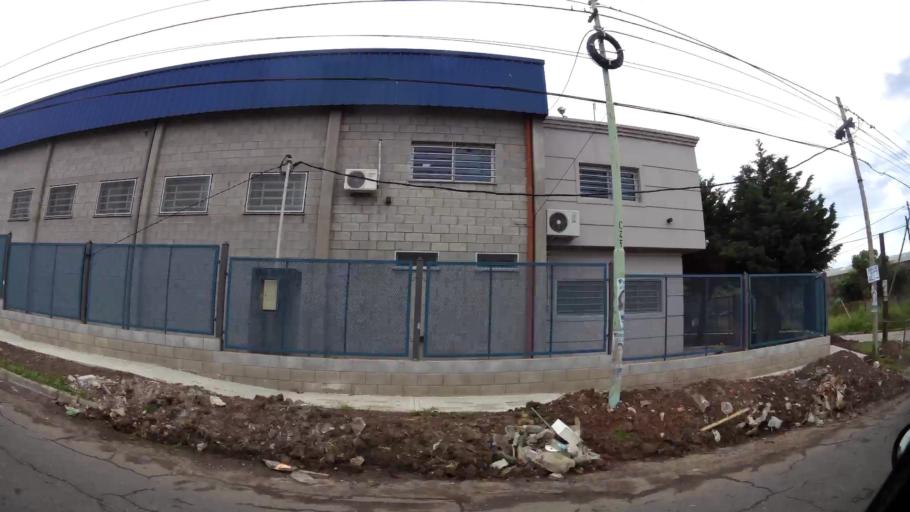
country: AR
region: Buenos Aires
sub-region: Partido de Quilmes
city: Quilmes
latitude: -34.7547
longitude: -58.2209
